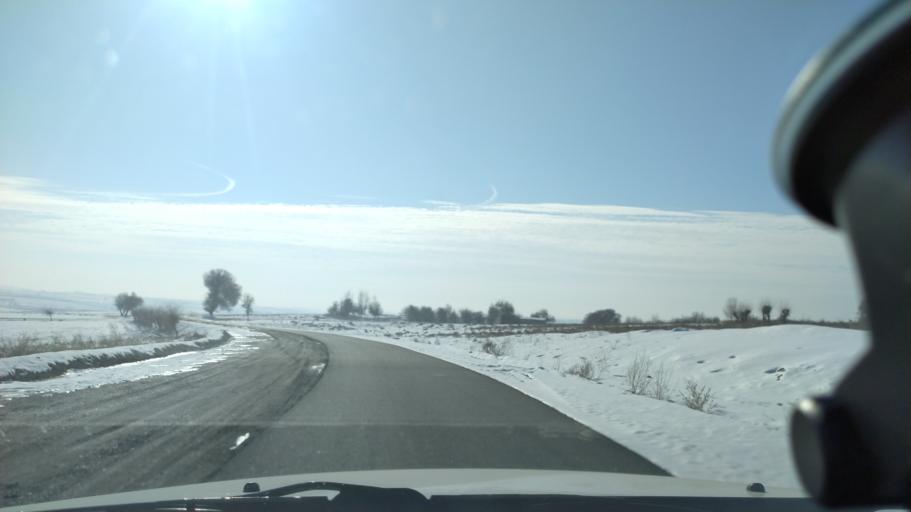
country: UZ
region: Namangan
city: Yangiqo`rg`on
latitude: 41.1490
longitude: 71.6568
